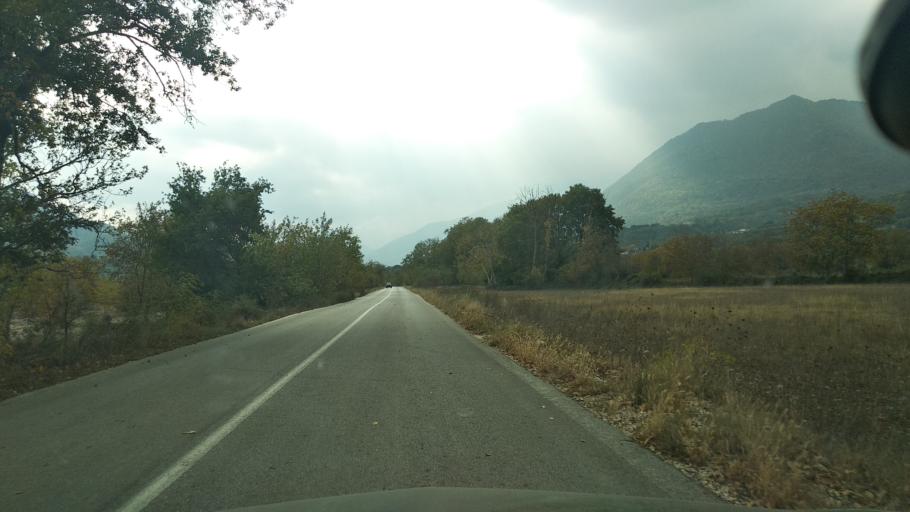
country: GR
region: Thessaly
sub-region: Trikala
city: Kastraki
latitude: 39.7009
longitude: 21.5256
